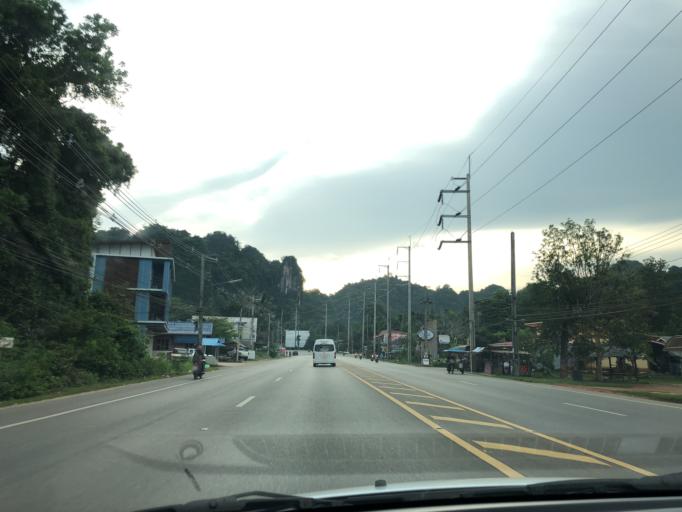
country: TH
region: Krabi
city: Krabi
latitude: 8.0865
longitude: 98.8824
